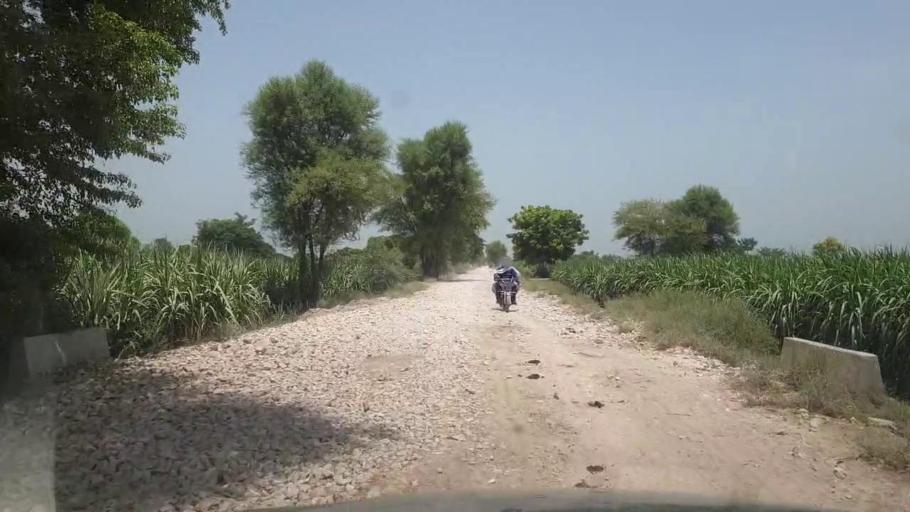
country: PK
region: Sindh
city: Sobhadero
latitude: 27.3249
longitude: 68.3505
